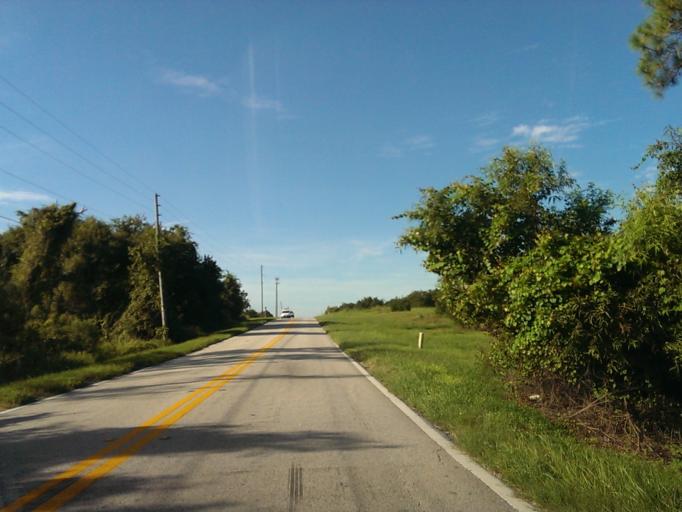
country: US
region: Florida
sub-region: Polk County
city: Citrus Ridge
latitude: 28.3811
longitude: -81.6427
